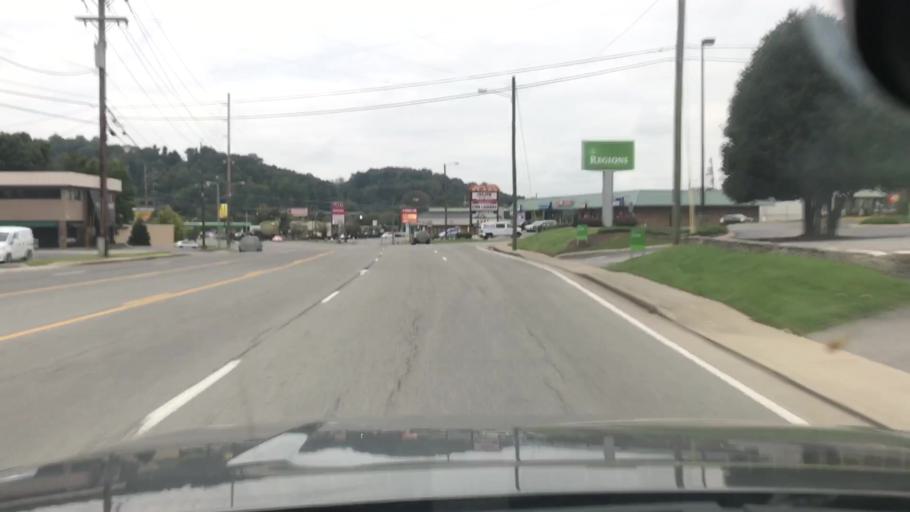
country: US
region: Tennessee
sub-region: Davidson County
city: Belle Meade
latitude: 36.0774
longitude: -86.9201
